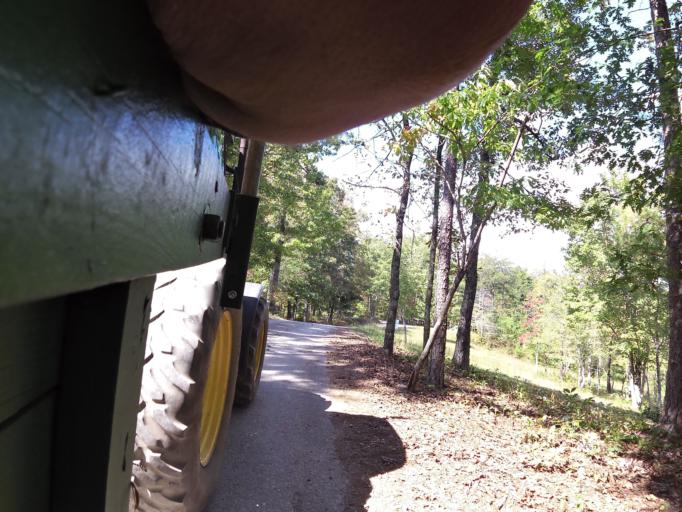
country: US
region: Georgia
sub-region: Dawson County
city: Dawsonville
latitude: 34.5470
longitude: -84.2537
